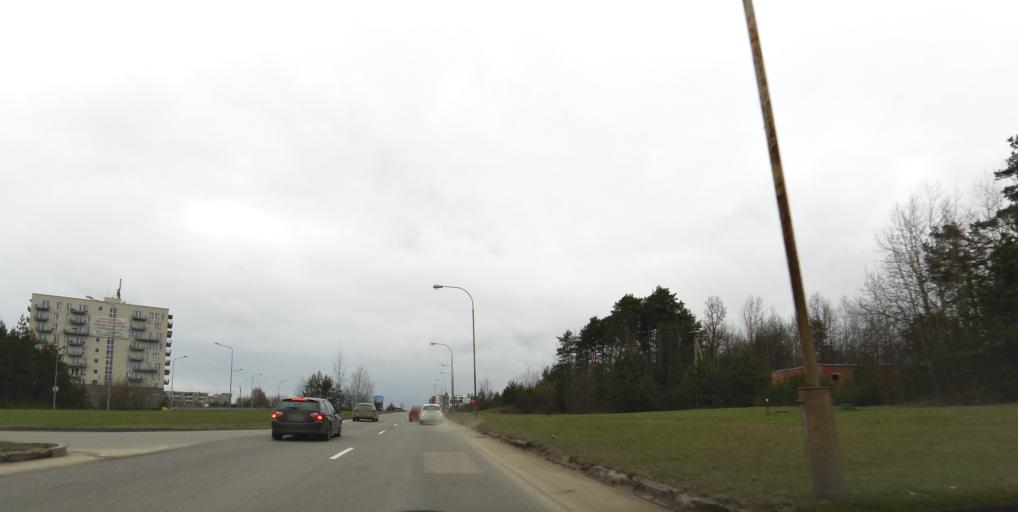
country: LT
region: Vilnius County
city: Pilaite
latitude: 54.7076
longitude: 25.1928
